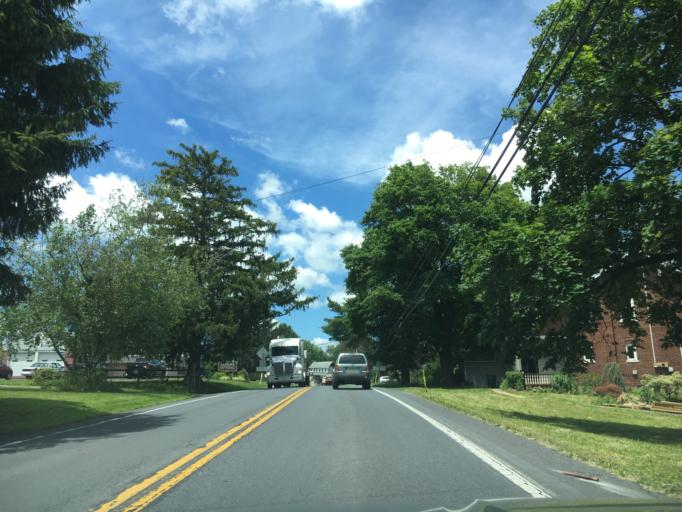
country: US
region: Pennsylvania
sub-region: Lehigh County
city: Laurys Station
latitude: 40.7223
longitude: -75.5288
